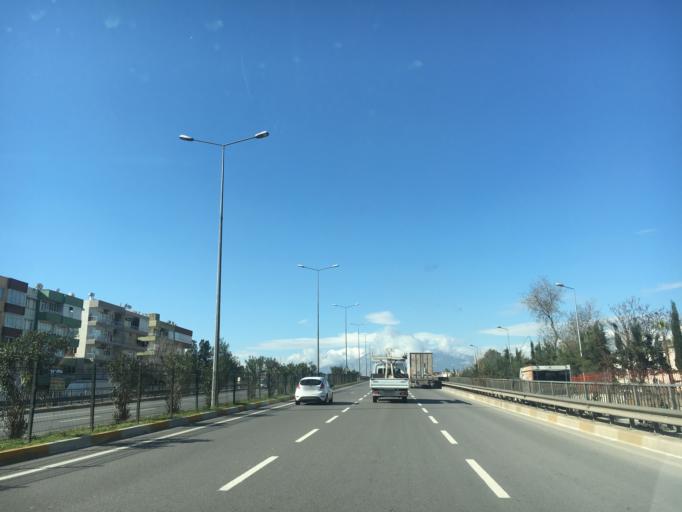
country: TR
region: Antalya
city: Antalya
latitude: 36.9116
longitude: 30.7004
